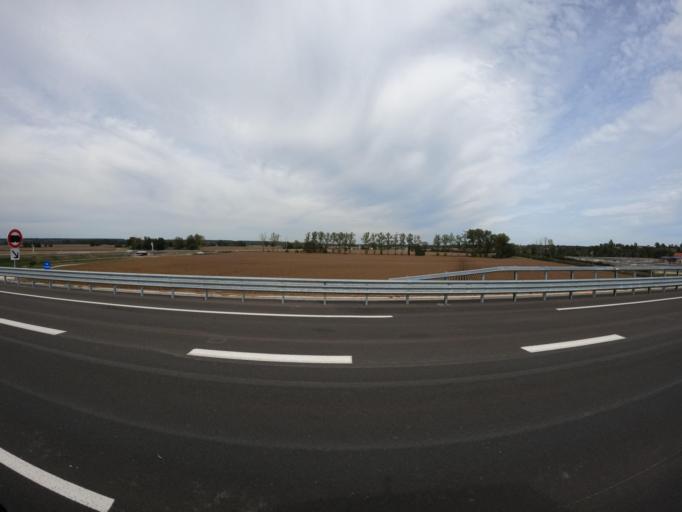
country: FR
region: Auvergne
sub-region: Departement de l'Allier
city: Toulon-sur-Allier
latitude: 46.4947
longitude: 3.3589
